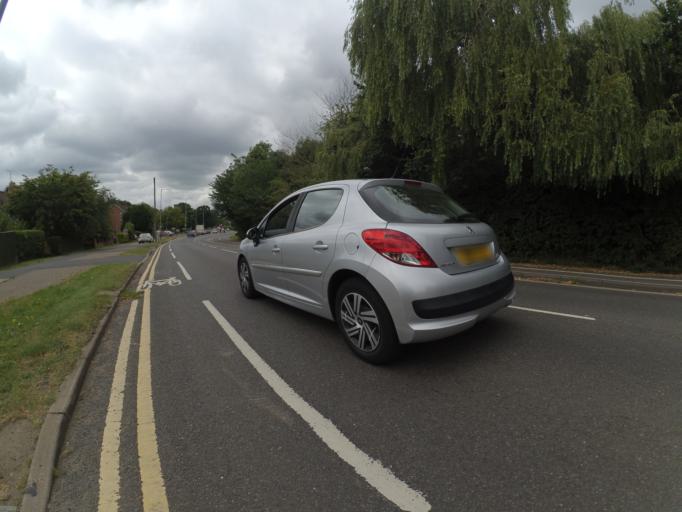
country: GB
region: England
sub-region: Warwickshire
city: Rugby
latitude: 52.3674
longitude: -1.2759
